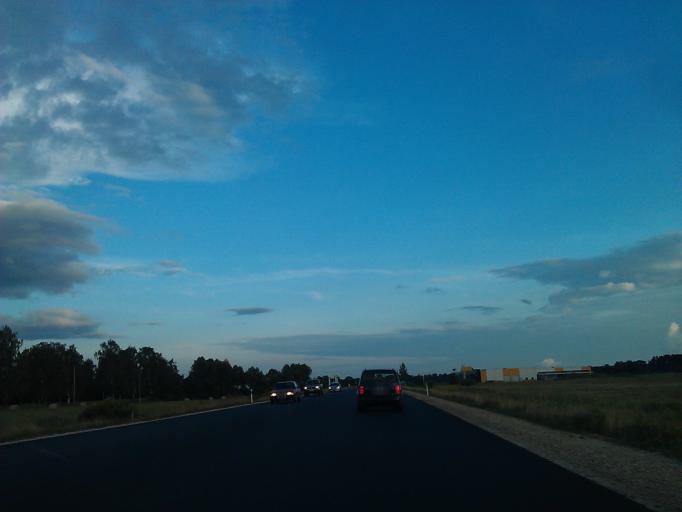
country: LV
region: Adazi
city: Adazi
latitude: 57.0929
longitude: 24.3123
